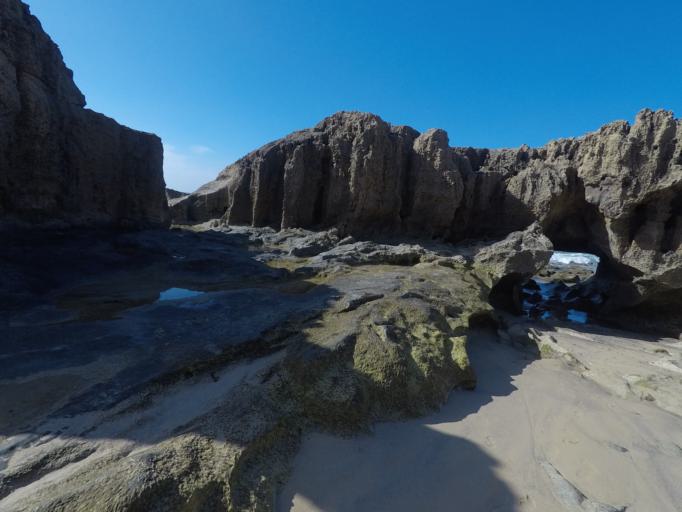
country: PT
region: Madeira
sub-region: Porto Santo
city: Vila de Porto Santo
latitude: 33.0244
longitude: -16.3795
